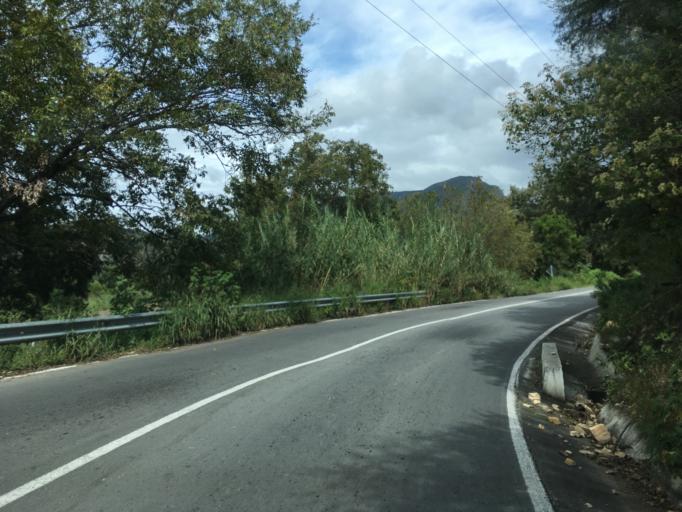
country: MX
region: Hidalgo
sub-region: San Agustin Metzquititlan
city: Mezquititlan
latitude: 20.5231
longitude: -98.7241
